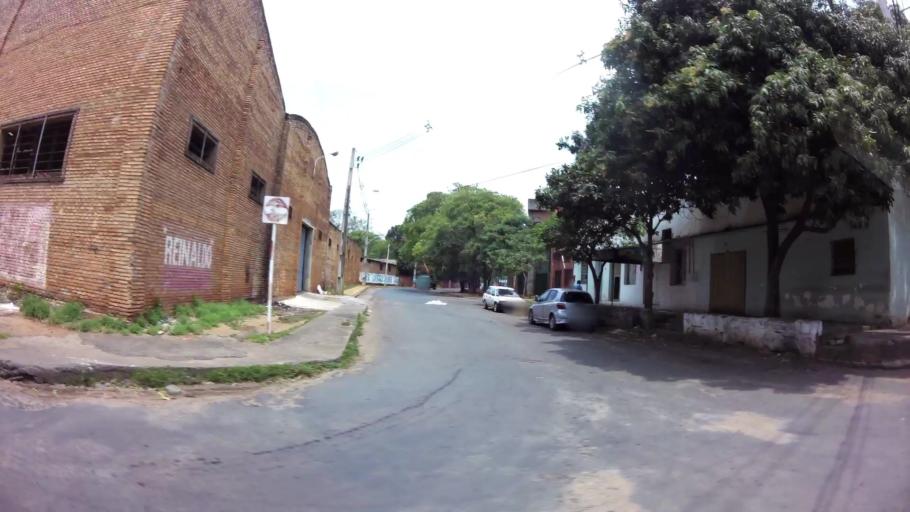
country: PY
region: Central
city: Lambare
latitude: -25.3163
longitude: -57.5672
